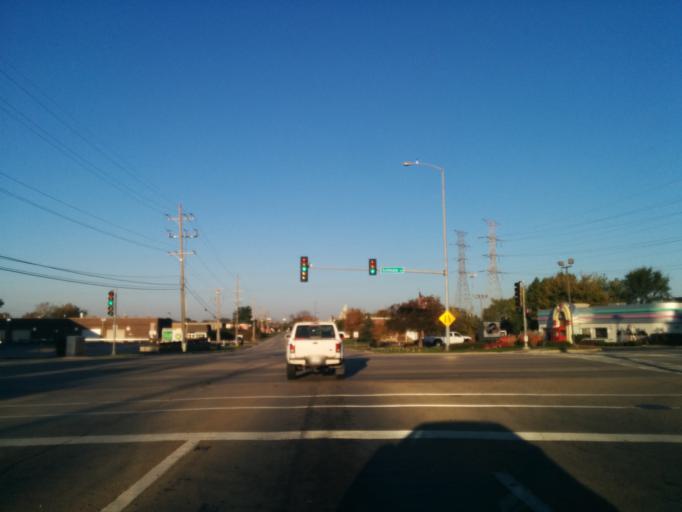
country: US
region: Illinois
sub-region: DuPage County
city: Wheaton
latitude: 41.8975
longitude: -88.1016
